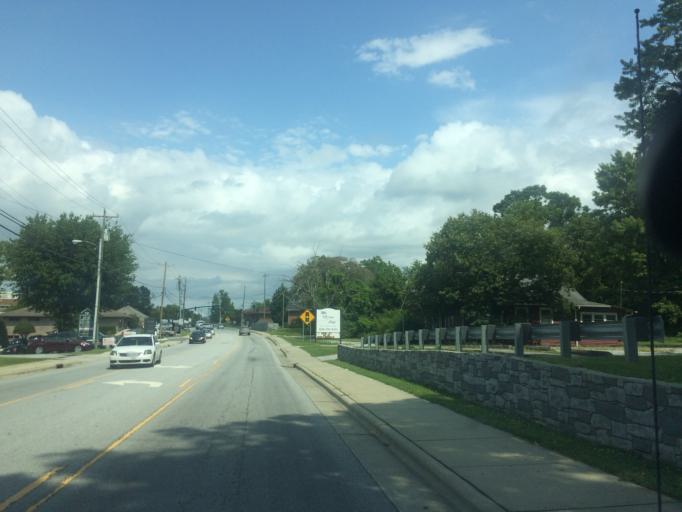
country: US
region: North Carolina
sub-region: Henderson County
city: Hendersonville
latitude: 35.3189
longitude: -82.4704
